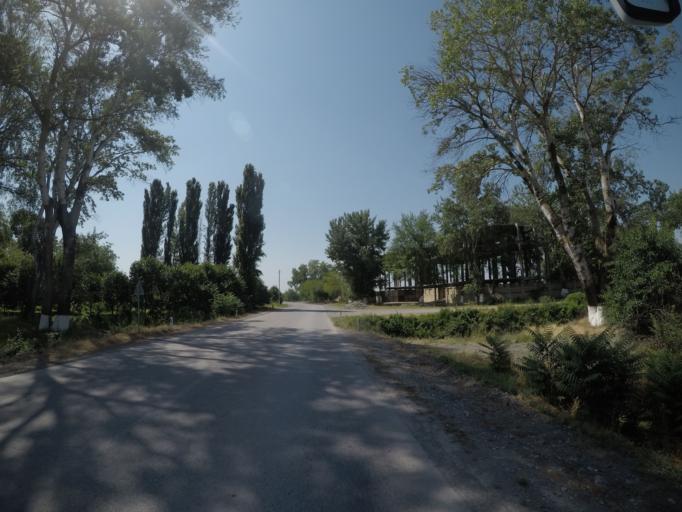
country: AZ
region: Agdas
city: Agdas
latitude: 40.7062
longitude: 47.5393
